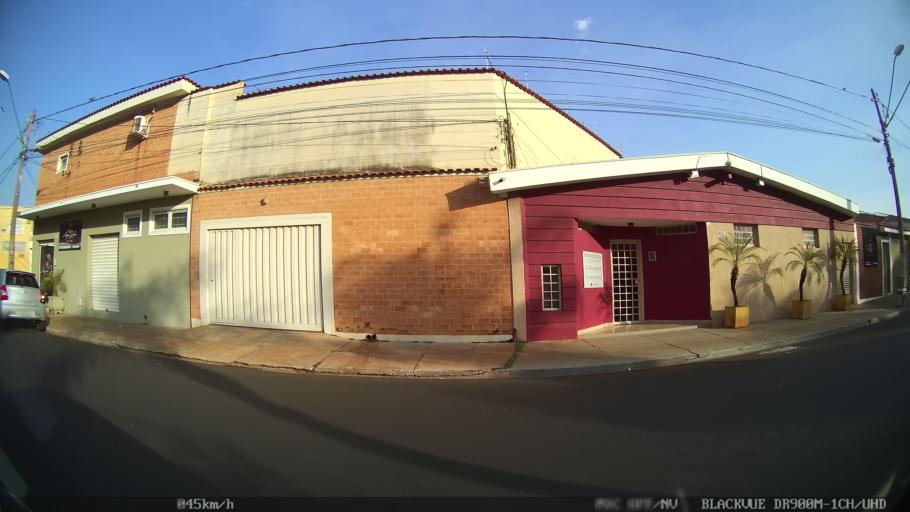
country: BR
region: Sao Paulo
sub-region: Ribeirao Preto
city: Ribeirao Preto
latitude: -21.1646
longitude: -47.8201
